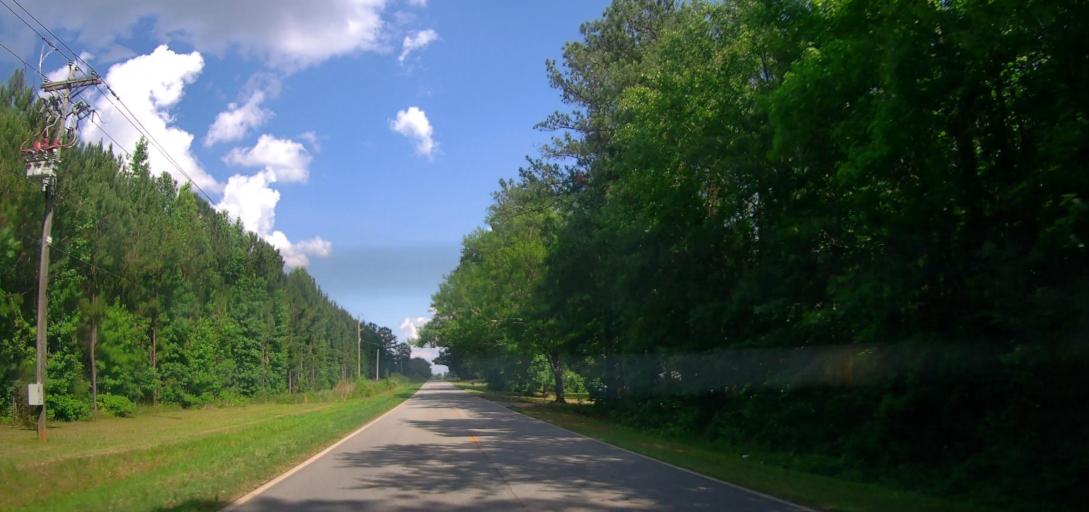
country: US
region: Georgia
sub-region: Henry County
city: Locust Grove
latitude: 33.2166
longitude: -84.0763
